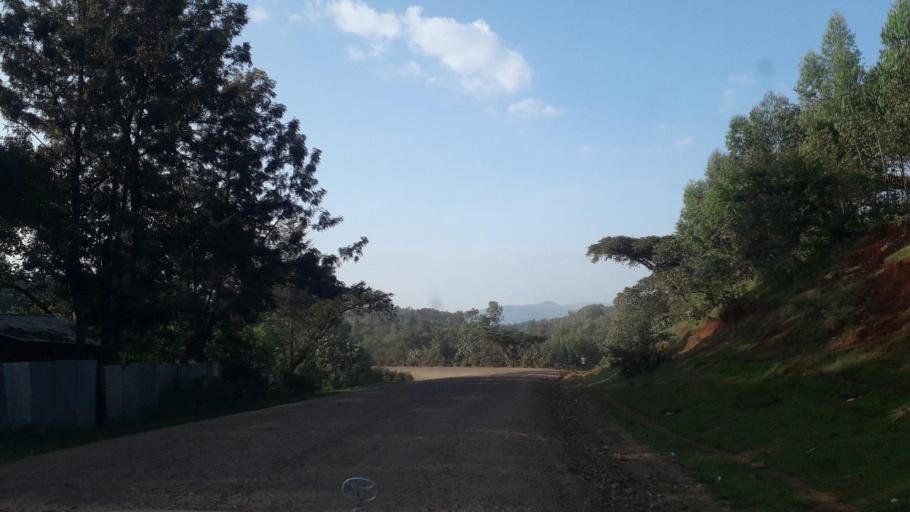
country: ET
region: Oromiya
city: Jima
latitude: 7.5832
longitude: 36.8581
